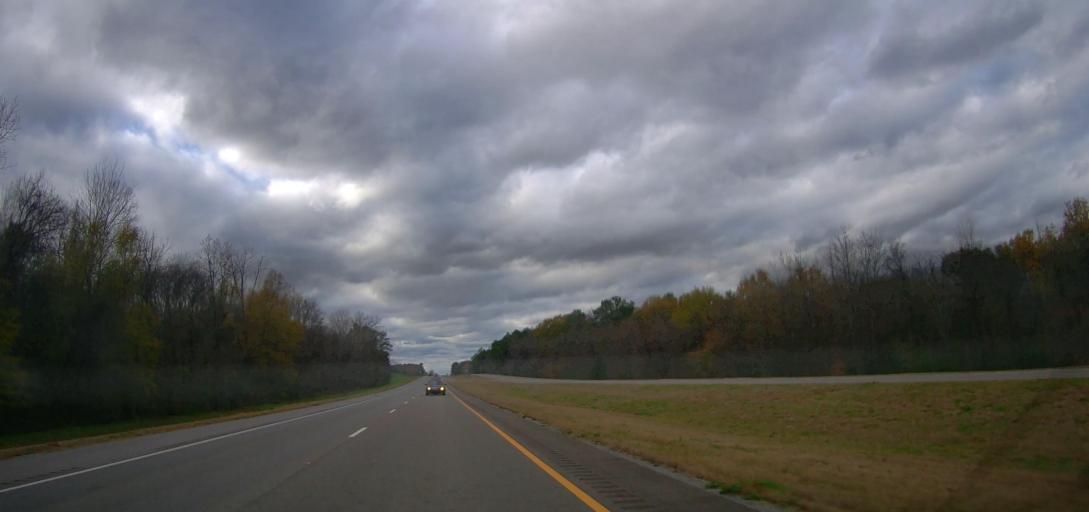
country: US
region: Alabama
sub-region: Morgan County
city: Danville
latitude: 34.3497
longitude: -87.0425
